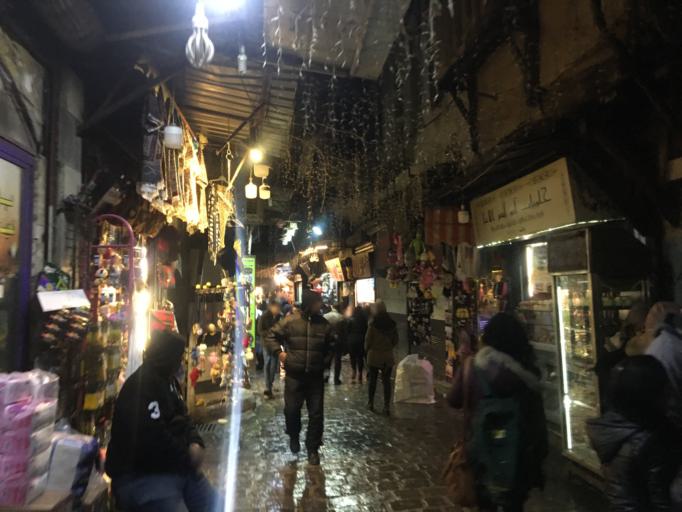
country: SY
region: Dimashq
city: Damascus
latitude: 33.5122
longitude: 36.3116
